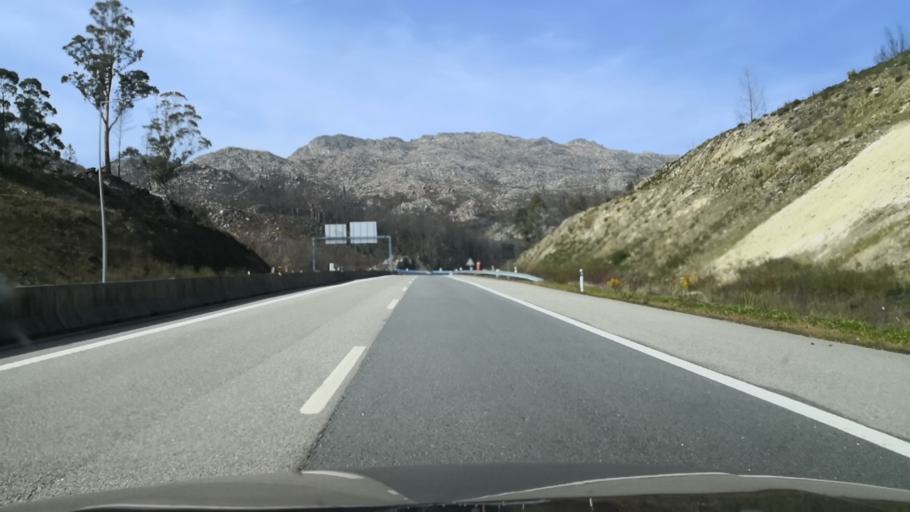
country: PT
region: Viseu
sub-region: Vouzela
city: Vouzela
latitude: 40.6512
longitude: -8.0723
